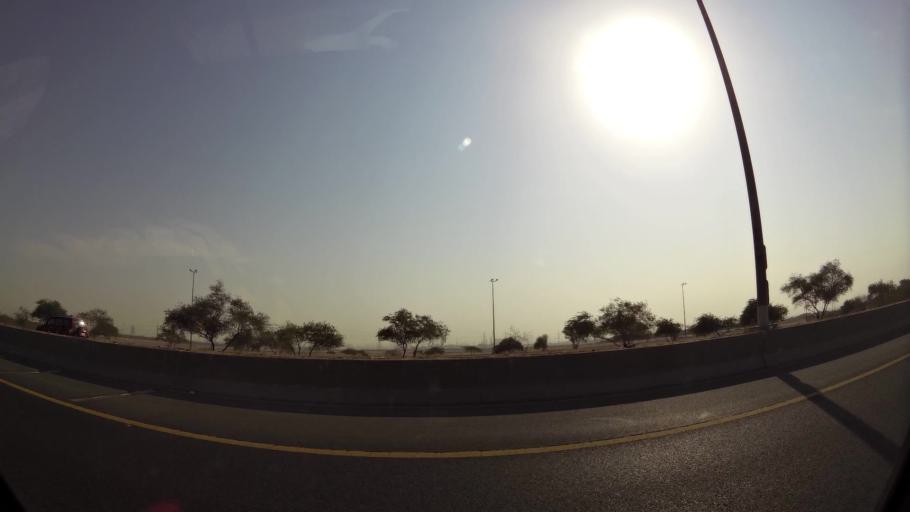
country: KW
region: Al Ahmadi
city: Al Ahmadi
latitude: 29.0545
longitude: 48.0963
